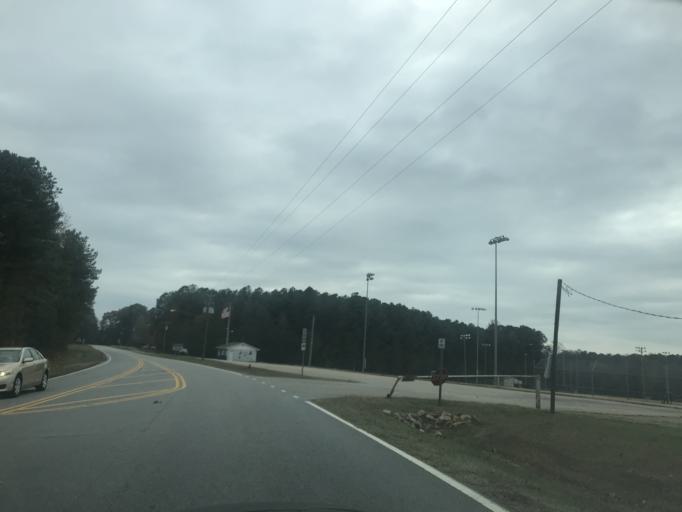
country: US
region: North Carolina
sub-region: Franklin County
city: Youngsville
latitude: 36.0224
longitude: -78.4835
